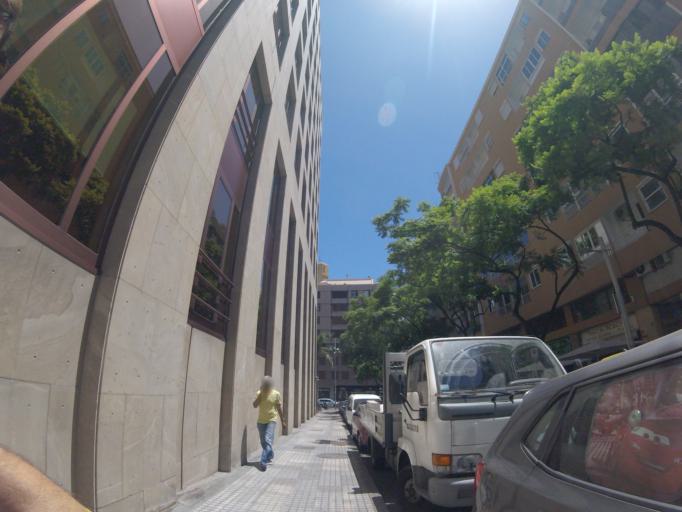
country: ES
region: Canary Islands
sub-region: Provincia de Santa Cruz de Tenerife
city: Santa Cruz de Tenerife
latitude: 28.4689
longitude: -16.2512
